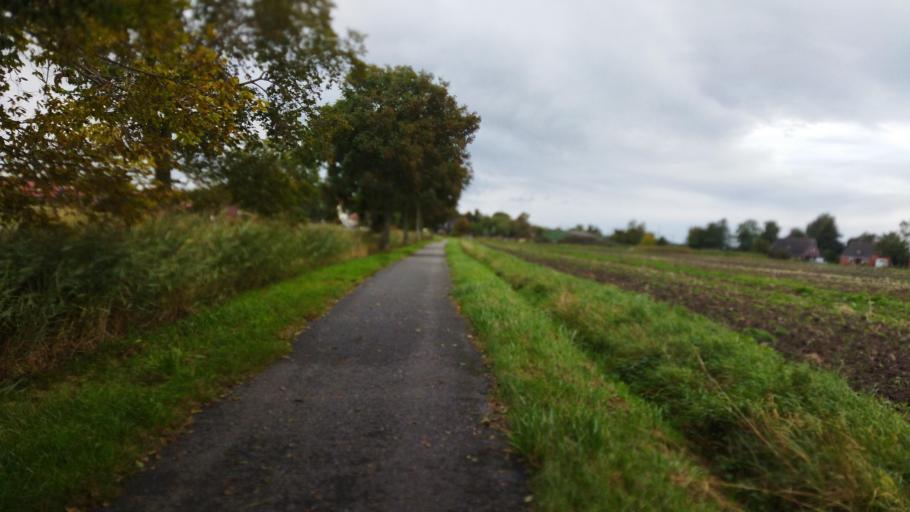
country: DE
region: Lower Saxony
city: Wirdum
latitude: 53.4765
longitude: 7.1382
